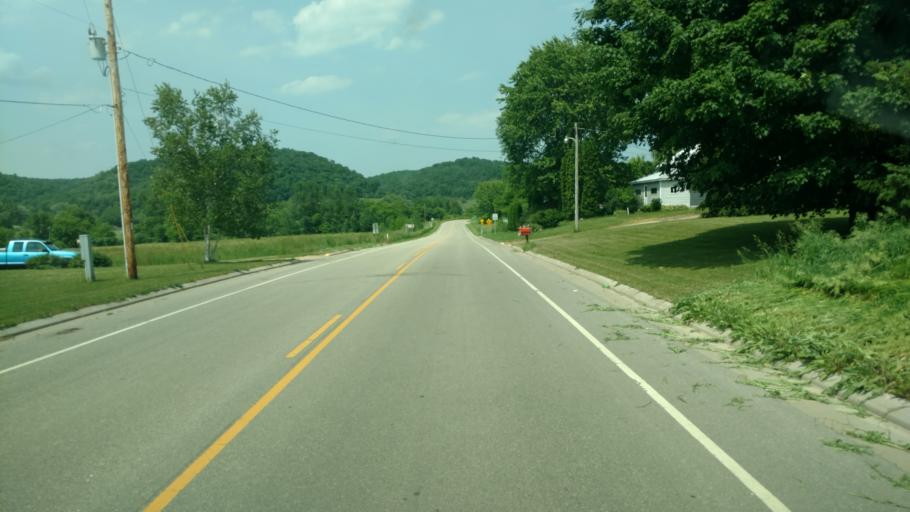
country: US
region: Wisconsin
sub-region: Vernon County
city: Viroqua
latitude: 43.4528
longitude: -90.7587
